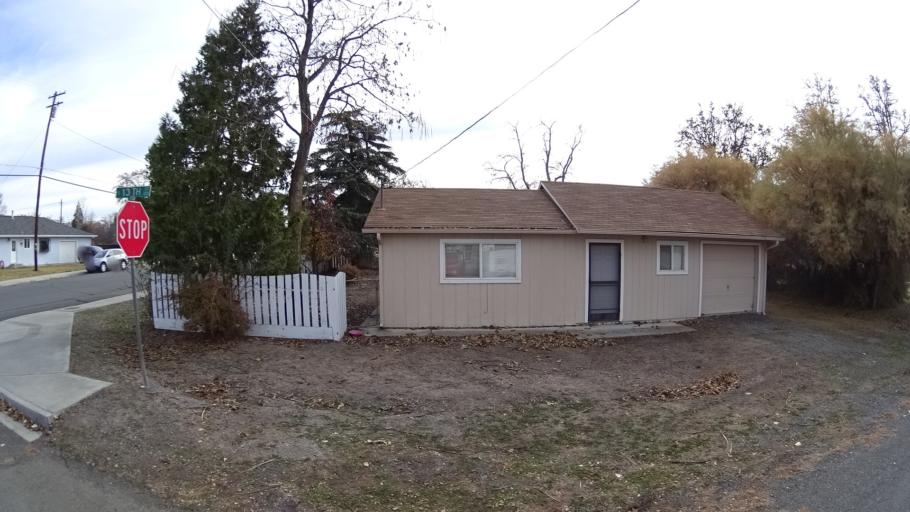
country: US
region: California
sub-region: Siskiyou County
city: Montague
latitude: 41.7290
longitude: -122.5303
